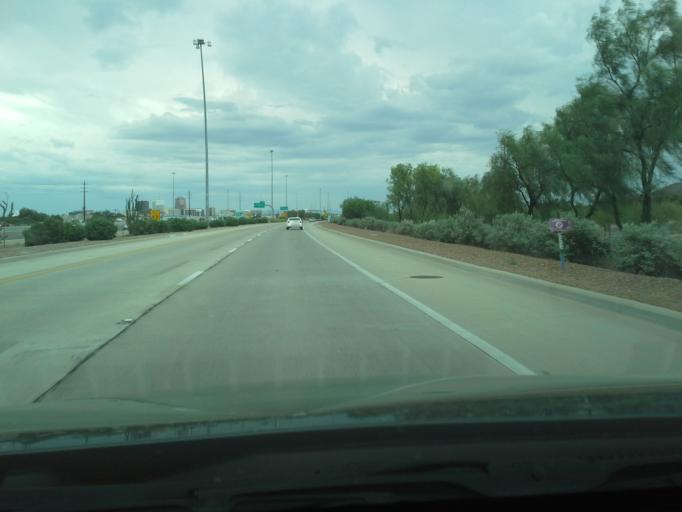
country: US
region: Arizona
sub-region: Pima County
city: South Tucson
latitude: 32.2413
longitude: -110.9865
